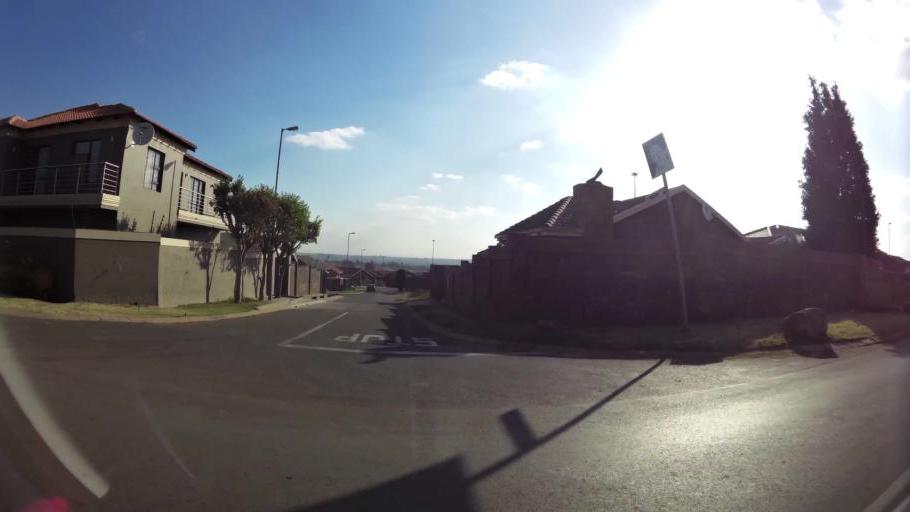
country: ZA
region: Gauteng
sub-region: City of Johannesburg Metropolitan Municipality
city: Soweto
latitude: -26.2641
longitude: 27.9168
